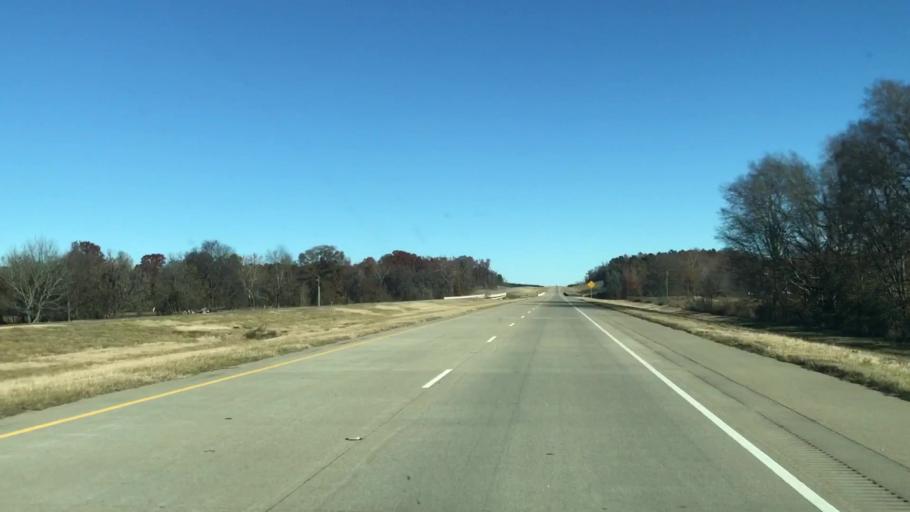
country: US
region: Louisiana
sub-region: Caddo Parish
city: Oil City
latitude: 32.7841
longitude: -93.8887
